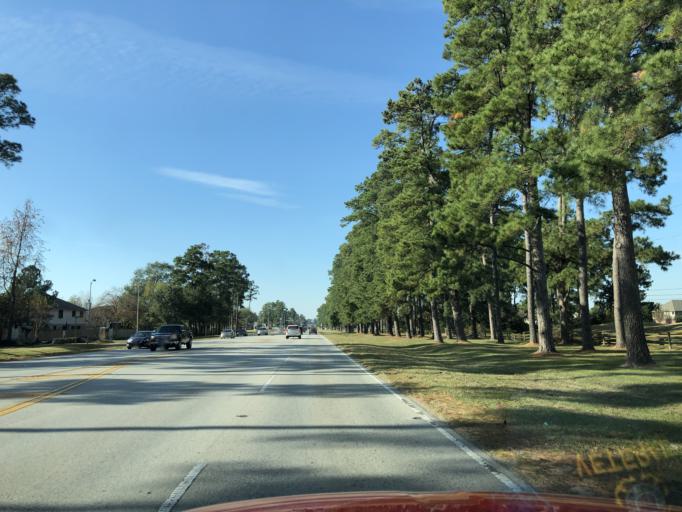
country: US
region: Texas
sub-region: Harris County
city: Tomball
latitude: 30.0291
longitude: -95.5596
